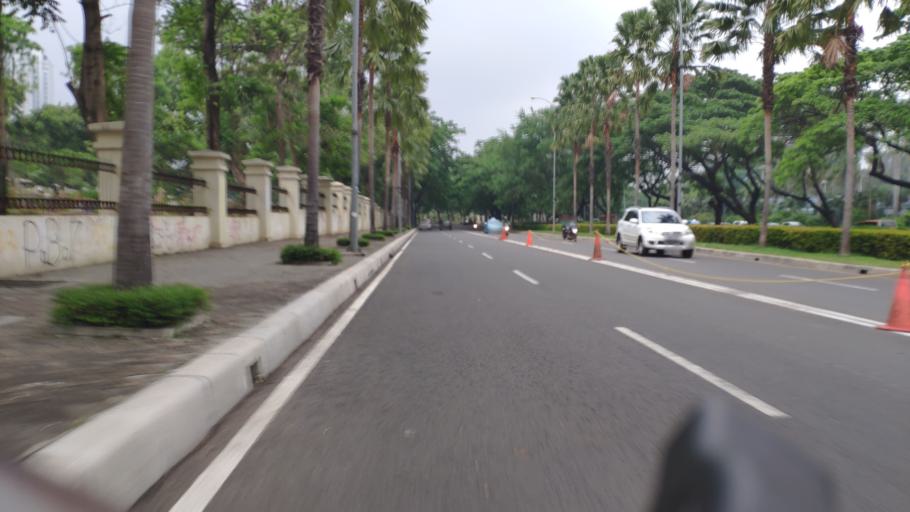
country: ID
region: Jakarta Raya
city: Jakarta
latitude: -6.2205
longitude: 106.8359
